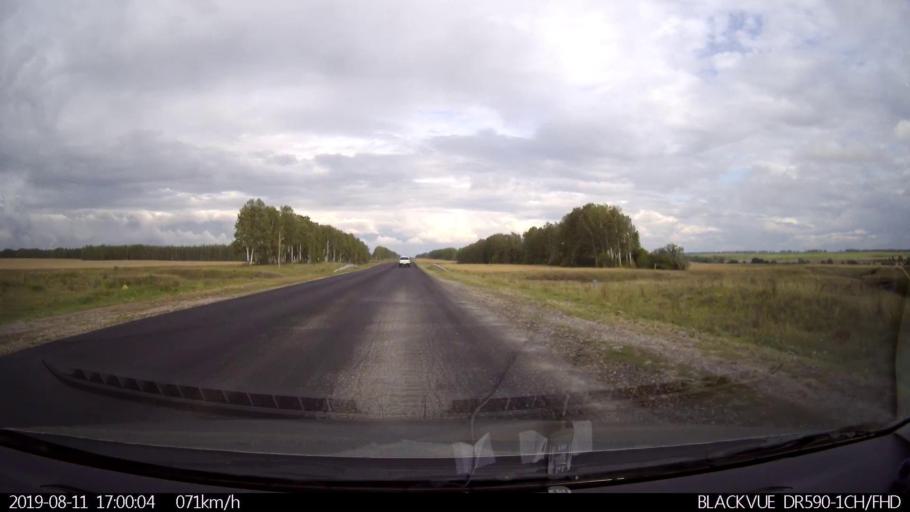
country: RU
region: Ulyanovsk
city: Mayna
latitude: 54.3112
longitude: 47.6729
